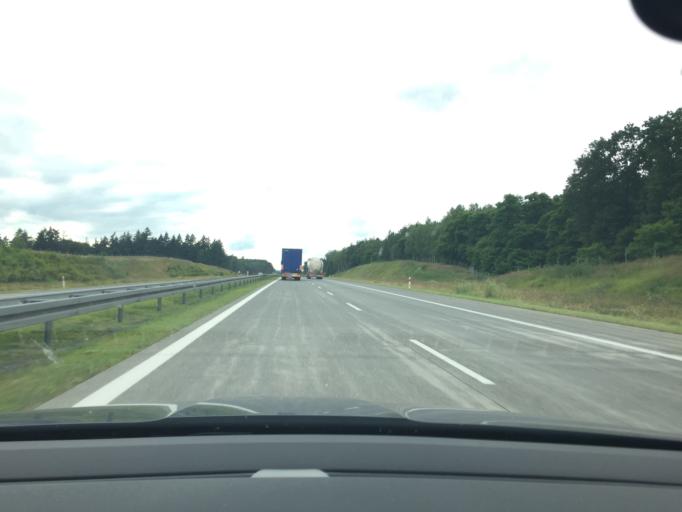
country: PL
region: Lubusz
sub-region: Powiat miedzyrzecki
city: Brojce
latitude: 52.3044
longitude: 15.6370
